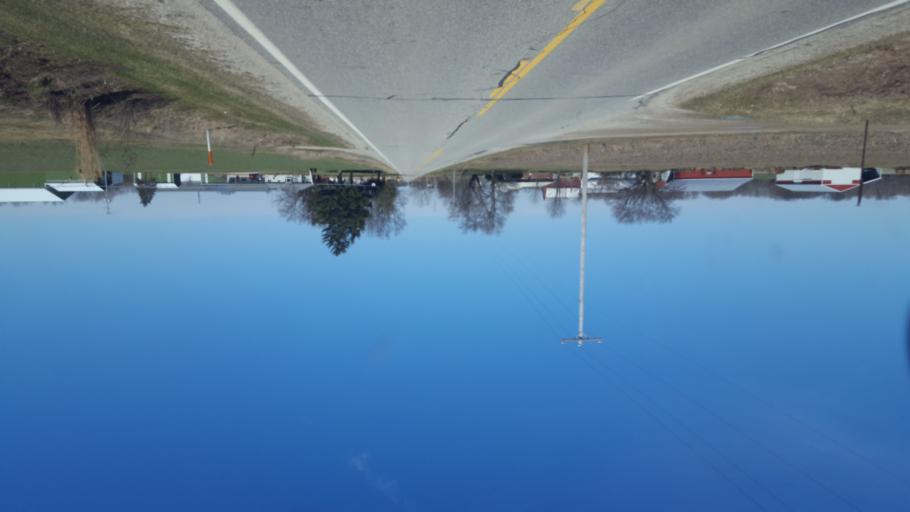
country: US
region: Michigan
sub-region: Montcalm County
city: Edmore
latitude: 43.4804
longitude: -85.0850
